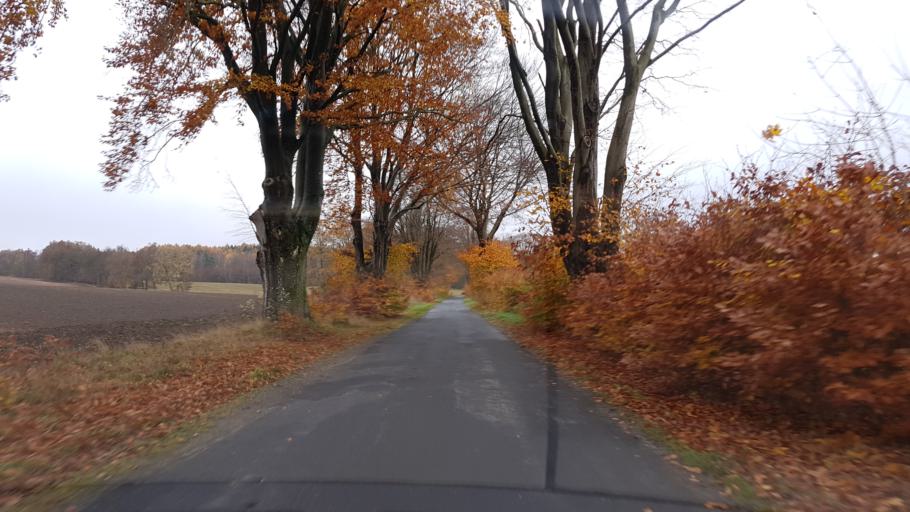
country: PL
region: West Pomeranian Voivodeship
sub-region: Powiat koszalinski
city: Polanow
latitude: 54.0859
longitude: 16.5946
